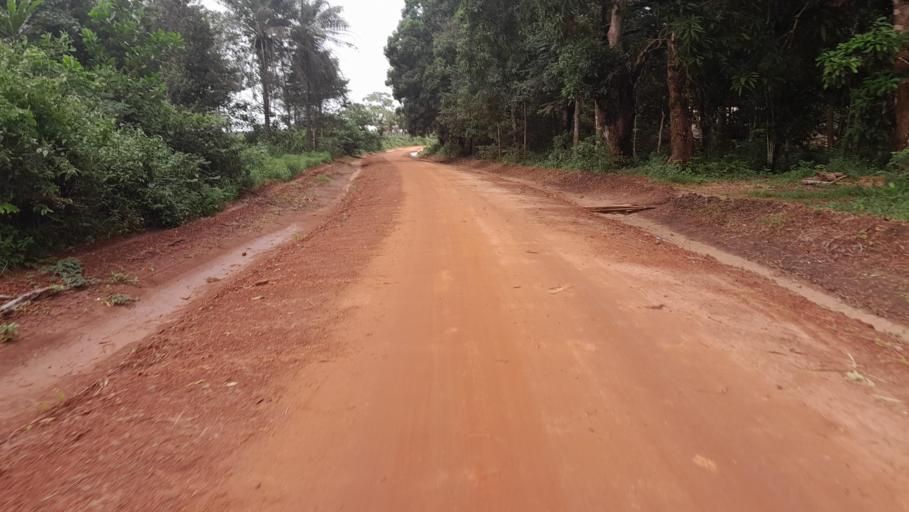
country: GN
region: Boke
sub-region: Boffa
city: Boffa
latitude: 10.0431
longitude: -13.8735
